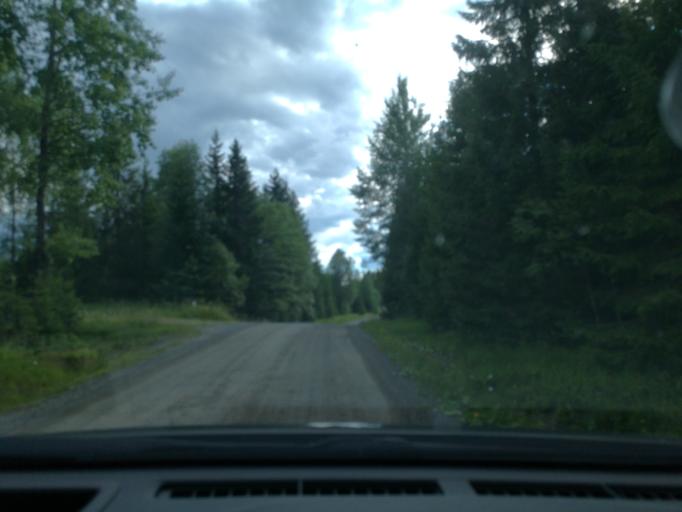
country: SE
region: Vaestmanland
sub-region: Surahammars Kommun
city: Ramnas
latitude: 59.8204
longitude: 16.2554
